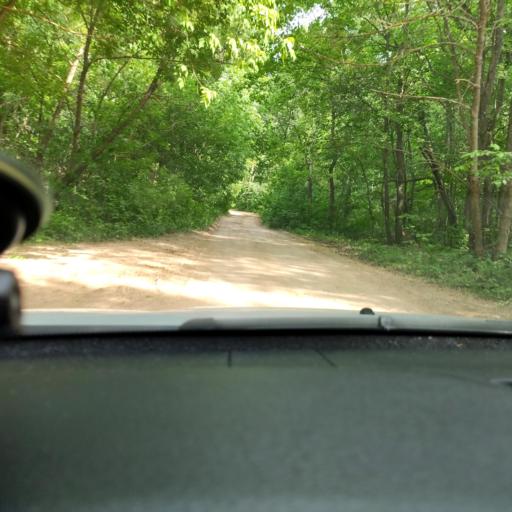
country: RU
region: Samara
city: Novosemeykino
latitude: 53.3359
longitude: 50.2252
